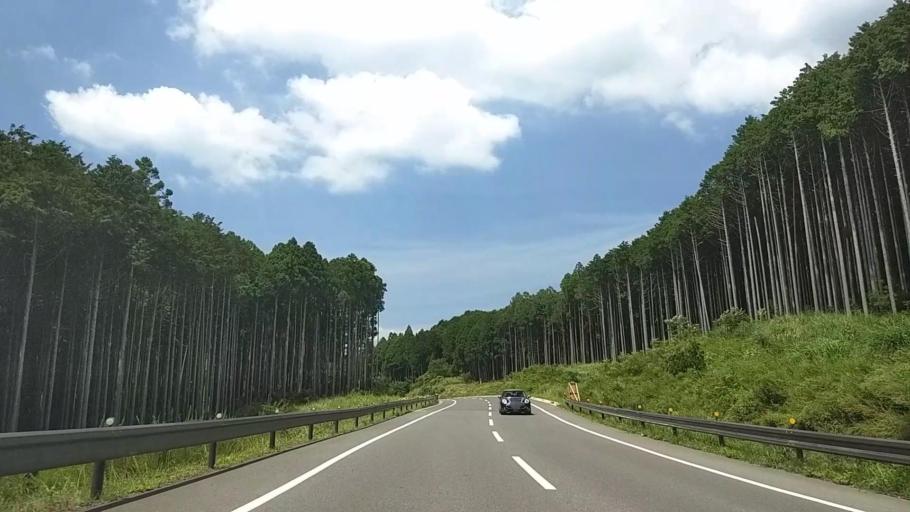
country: JP
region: Shizuoka
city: Fujinomiya
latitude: 35.2546
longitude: 138.6827
